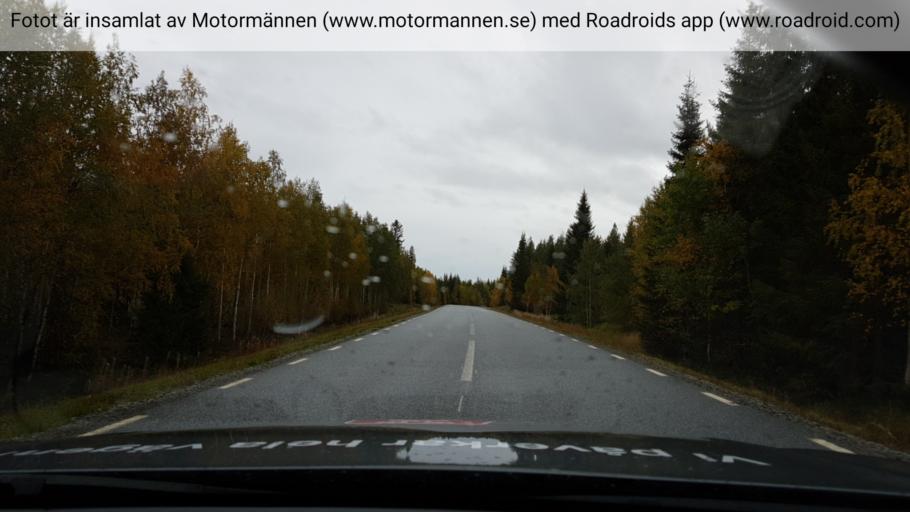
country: SE
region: Vaesterbotten
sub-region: Vilhelmina Kommun
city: Sjoberg
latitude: 64.8295
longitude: 15.9463
